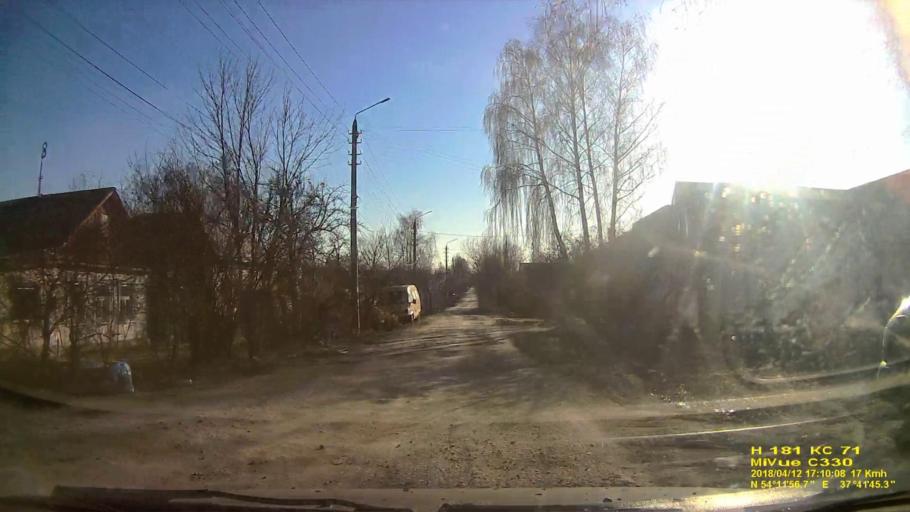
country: RU
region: Tula
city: Tula
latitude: 54.1991
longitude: 37.6959
